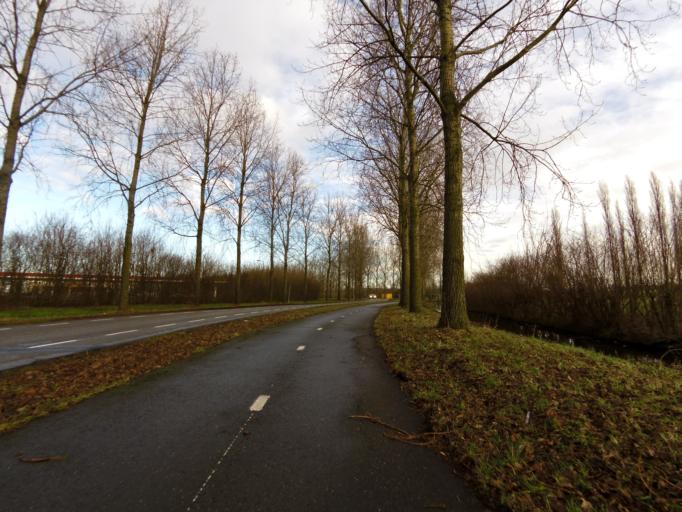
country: NL
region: South Holland
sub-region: Gemeente Delft
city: Delft
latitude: 51.9822
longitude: 4.3959
